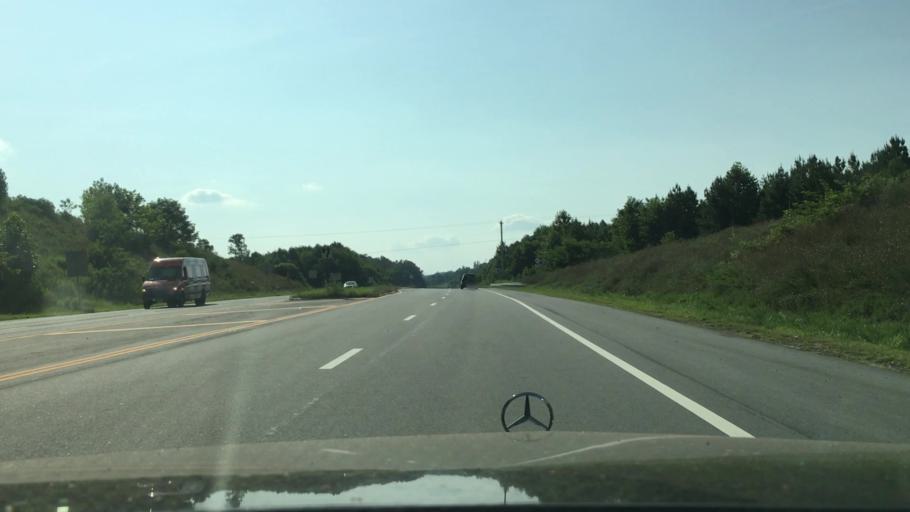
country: US
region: Virginia
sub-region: Amherst County
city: Madison Heights
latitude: 37.4088
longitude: -79.0869
